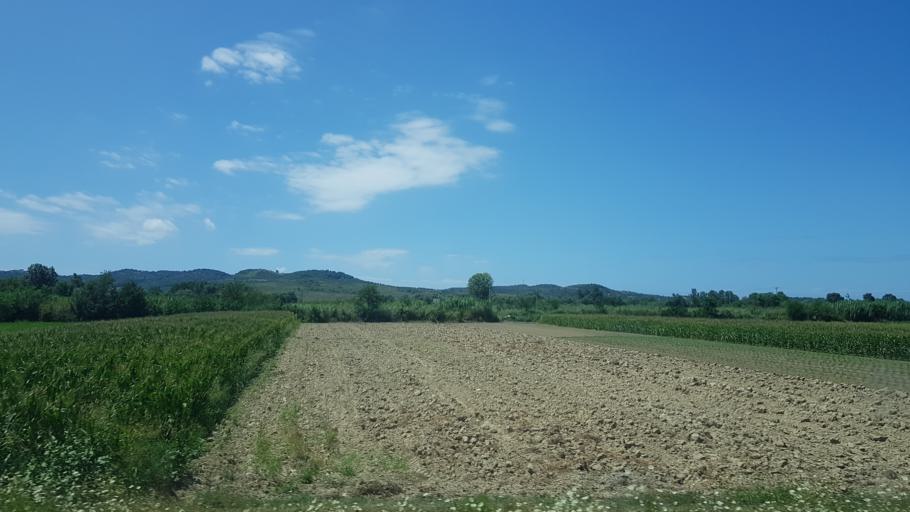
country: AL
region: Fier
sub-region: Rrethi i Fierit
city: Frakulla e Madhe
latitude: 40.6128
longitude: 19.5237
